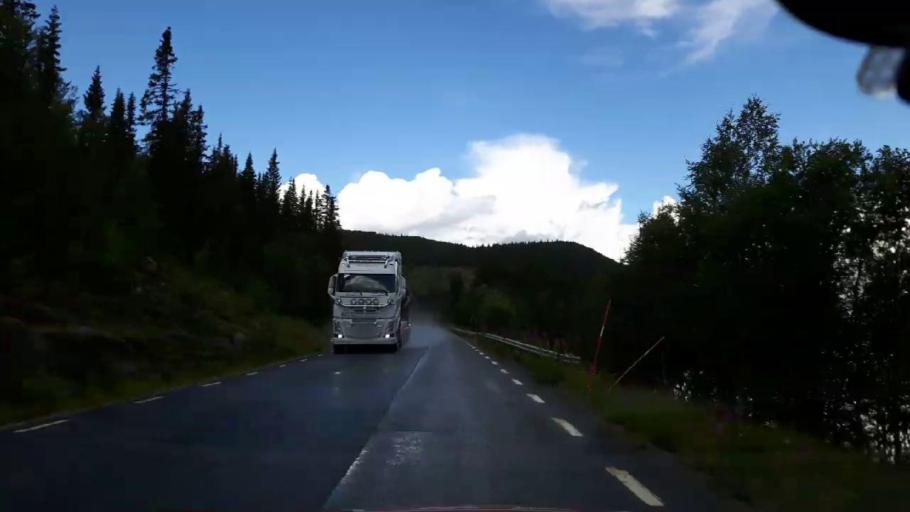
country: SE
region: Vaesterbotten
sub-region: Vilhelmina Kommun
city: Sjoberg
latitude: 64.9953
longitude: 15.2159
